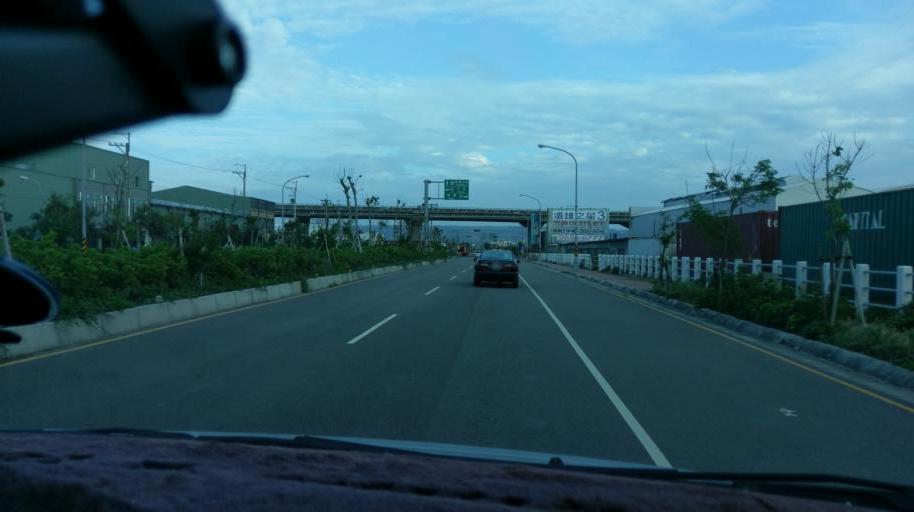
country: TW
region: Taiwan
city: Fengyuan
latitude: 24.2950
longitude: 120.5510
